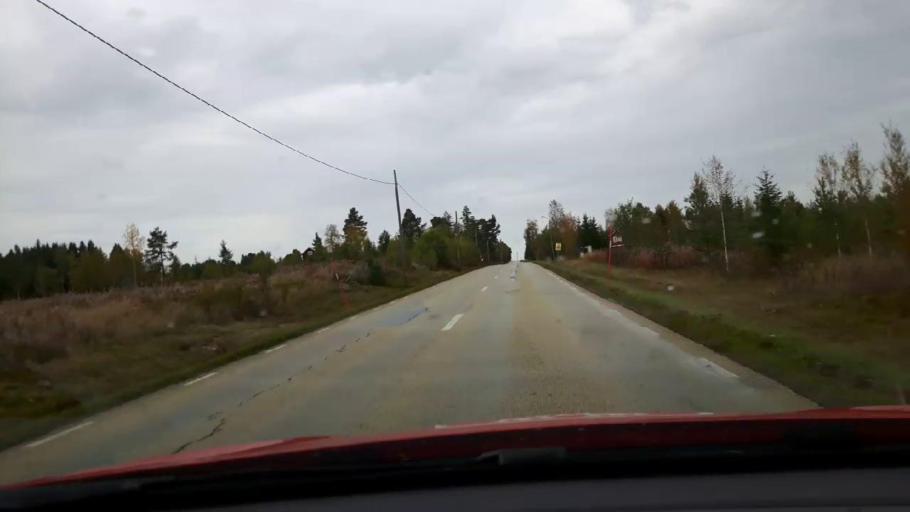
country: SE
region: Jaemtland
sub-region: Bergs Kommun
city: Hoverberg
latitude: 62.9820
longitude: 14.3435
